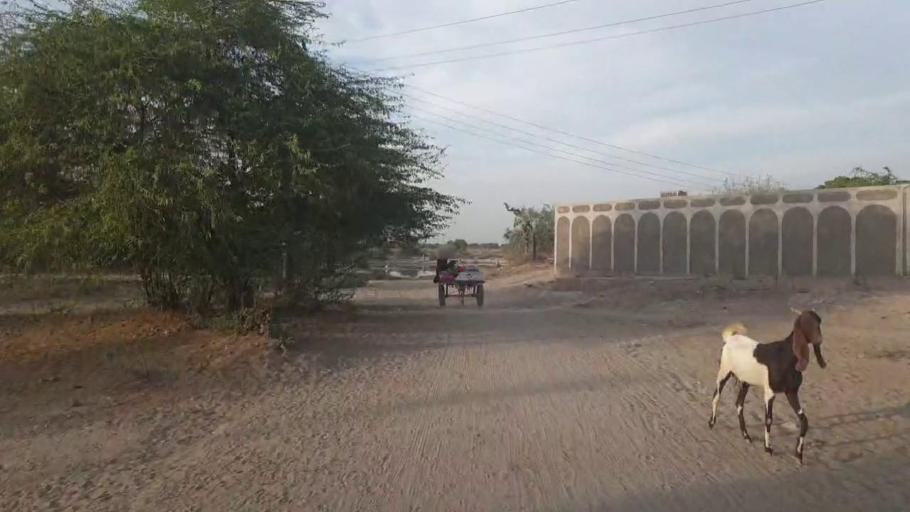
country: PK
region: Sindh
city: Nabisar
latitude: 25.1548
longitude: 69.6794
